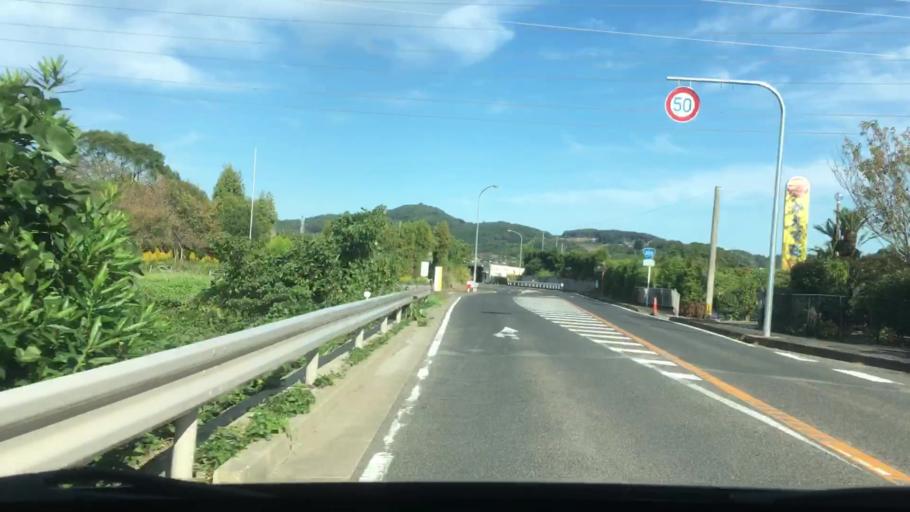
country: JP
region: Nagasaki
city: Sasebo
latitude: 33.0746
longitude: 129.7601
